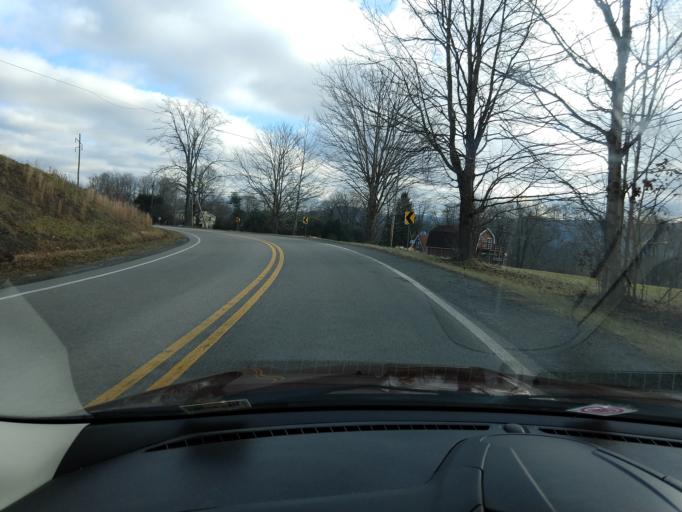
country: US
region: West Virginia
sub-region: Randolph County
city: Elkins
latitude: 38.7837
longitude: -79.9091
